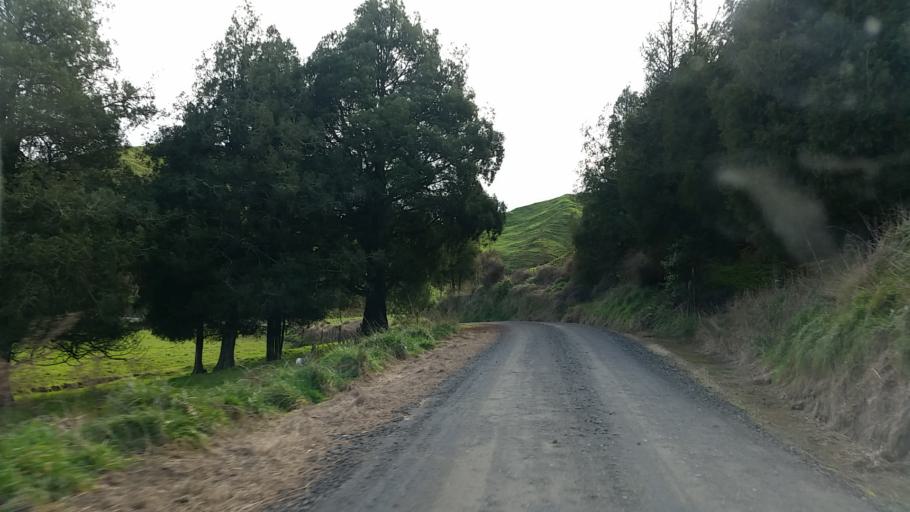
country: NZ
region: Taranaki
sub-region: South Taranaki District
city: Eltham
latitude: -39.2561
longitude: 174.5243
